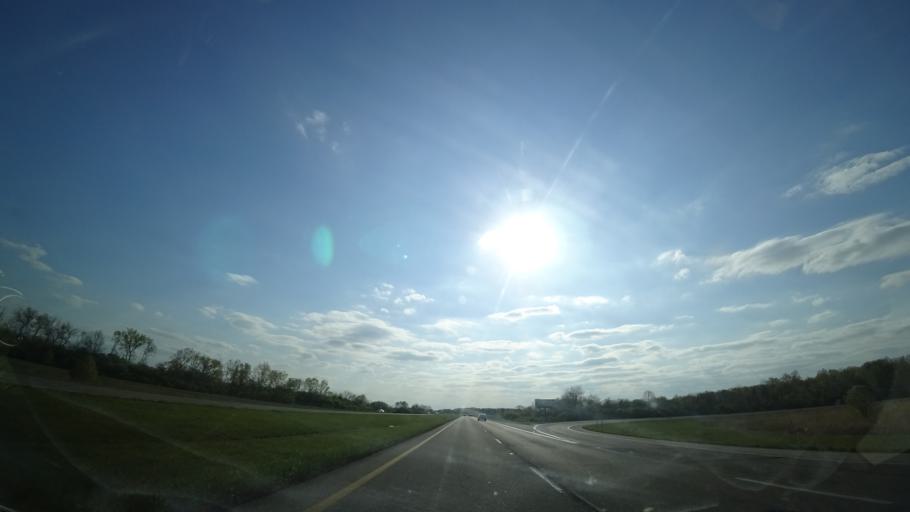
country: US
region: Ohio
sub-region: Montgomery County
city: Riverside
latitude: 39.7999
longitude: -84.1037
